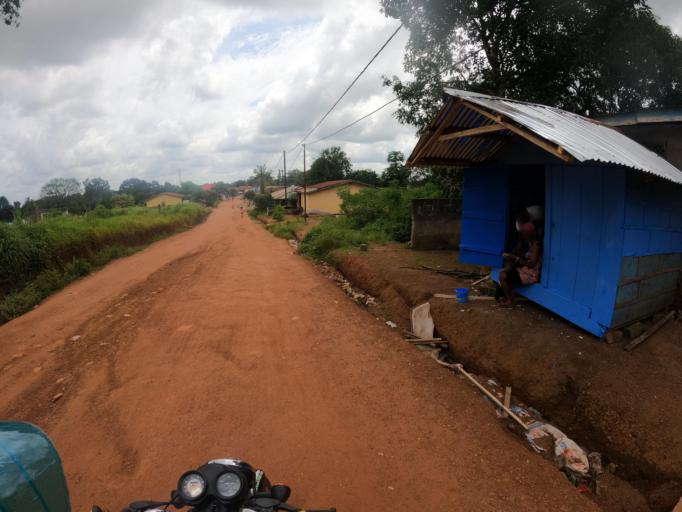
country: SL
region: Northern Province
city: Makeni
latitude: 8.9015
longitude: -12.0438
